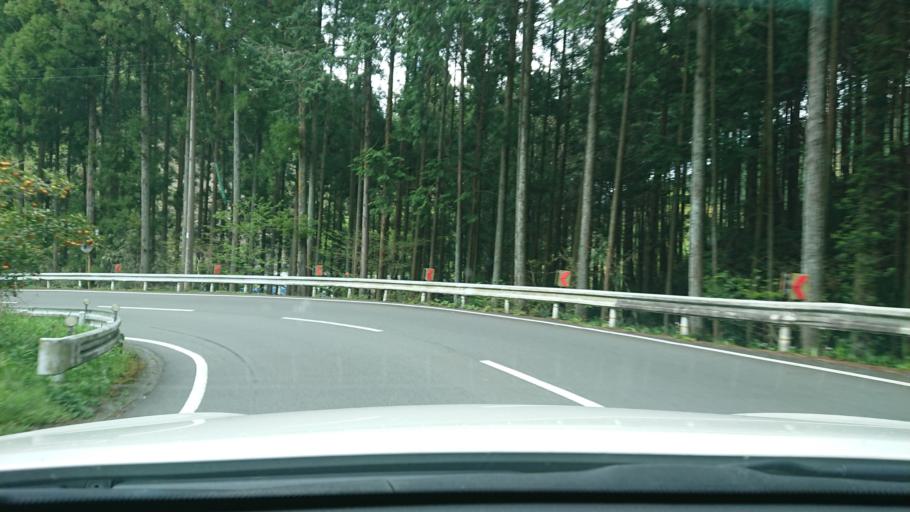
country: JP
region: Tokushima
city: Ishii
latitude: 33.9161
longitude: 134.4252
